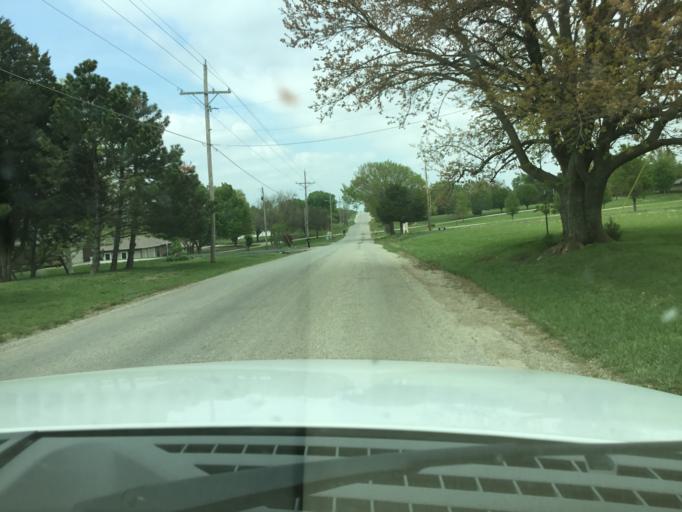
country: US
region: Kansas
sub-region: Shawnee County
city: Topeka
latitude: 39.0259
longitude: -95.5858
